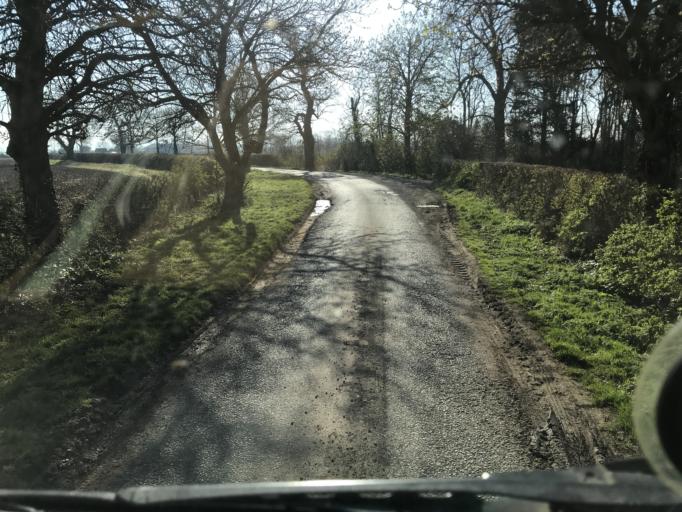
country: GB
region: England
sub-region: Cheshire West and Chester
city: Aldford
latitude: 53.1271
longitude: -2.8570
